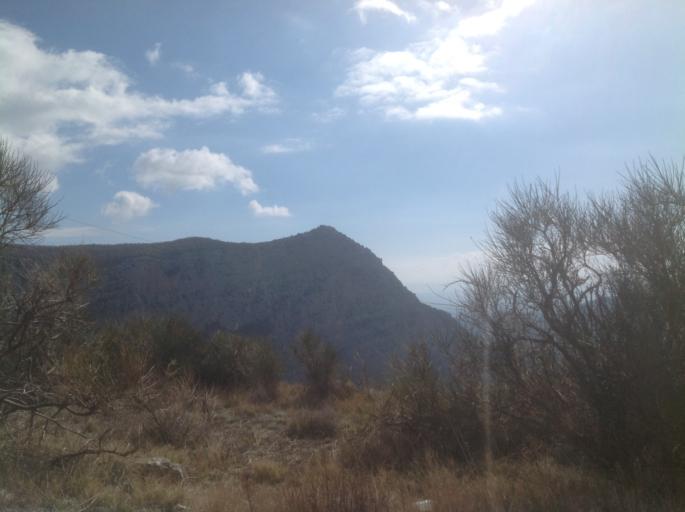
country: IT
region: Calabria
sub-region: Provincia di Cosenza
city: Civita
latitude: 39.8417
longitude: 16.3076
